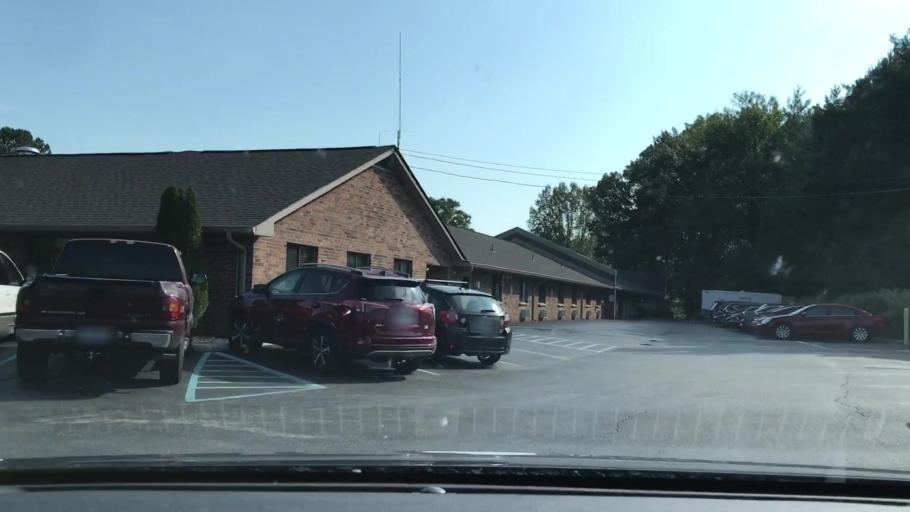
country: US
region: Kentucky
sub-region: Pulaski County
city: Somerset
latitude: 37.0721
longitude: -84.6143
